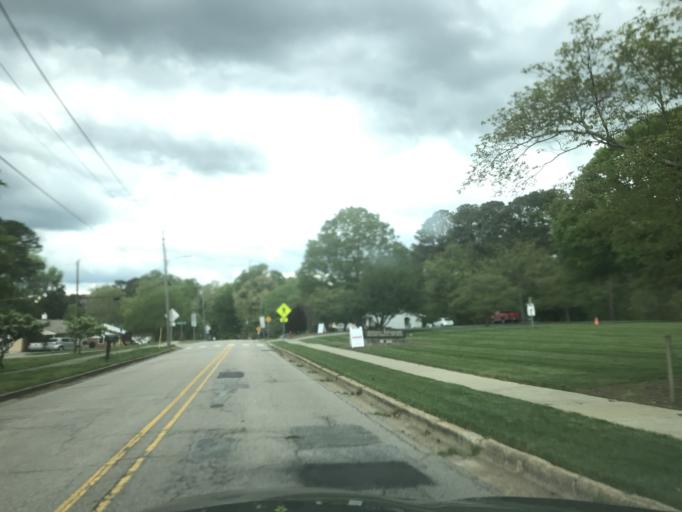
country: US
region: North Carolina
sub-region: Wake County
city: West Raleigh
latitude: 35.7773
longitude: -78.7040
